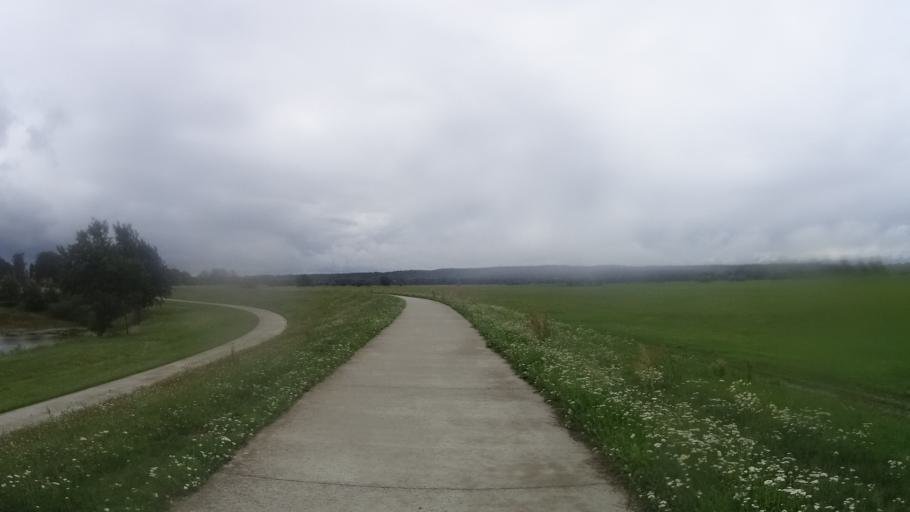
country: DE
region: Lower Saxony
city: Tosterglope
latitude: 53.2776
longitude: 10.8250
